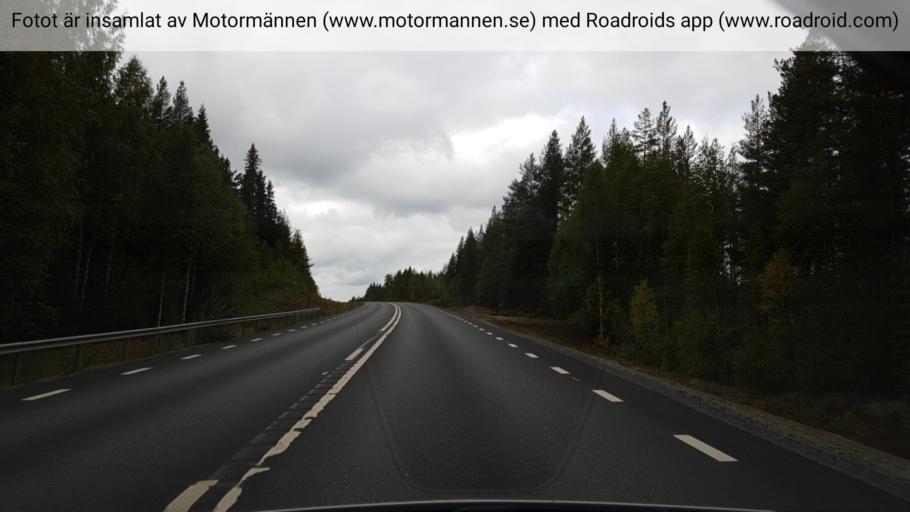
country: SE
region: Vaesterbotten
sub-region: Norsjo Kommun
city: Norsjoe
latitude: 64.9654
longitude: 19.8597
